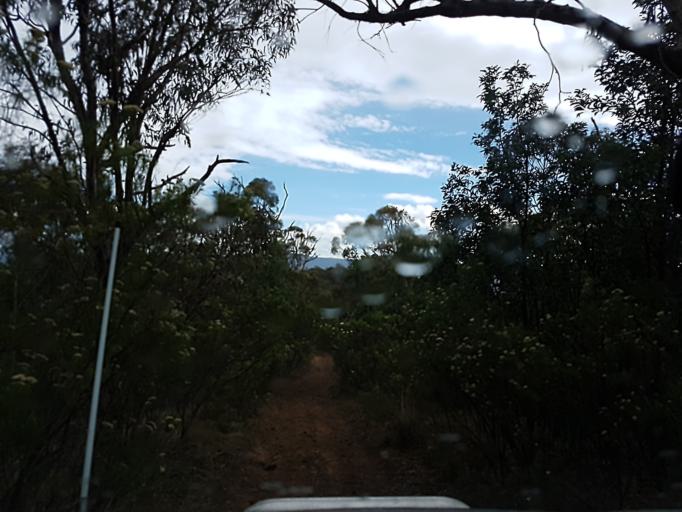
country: AU
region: New South Wales
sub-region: Snowy River
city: Jindabyne
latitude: -36.9086
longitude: 148.3389
